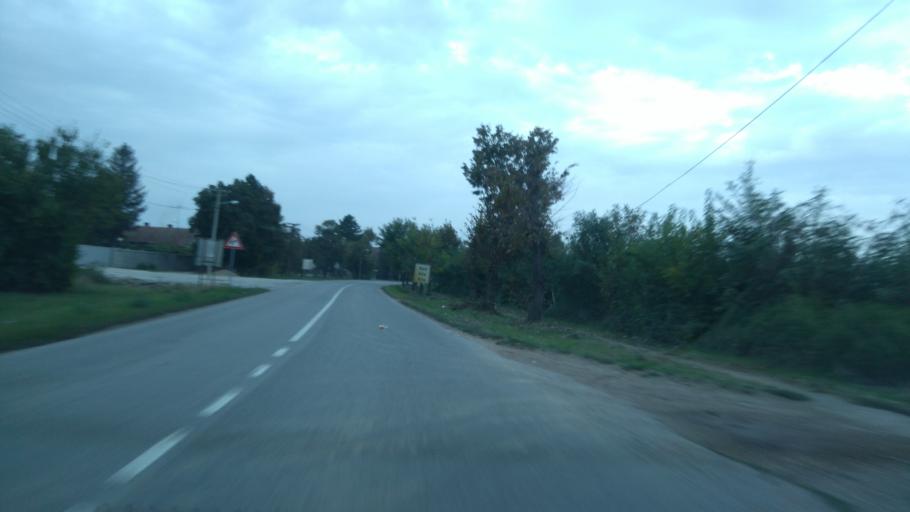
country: RS
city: Mol
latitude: 45.7793
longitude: 20.1355
